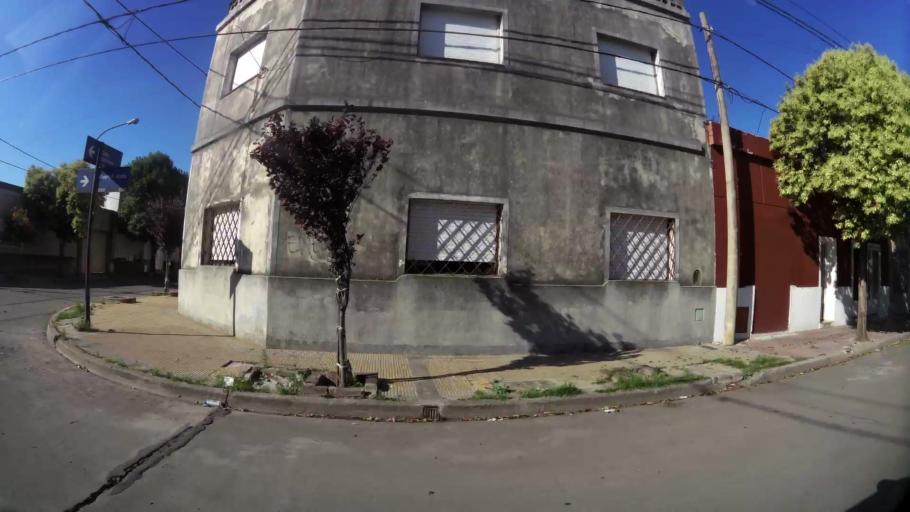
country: AR
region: Cordoba
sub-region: Departamento de Capital
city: Cordoba
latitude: -31.3939
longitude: -64.1685
